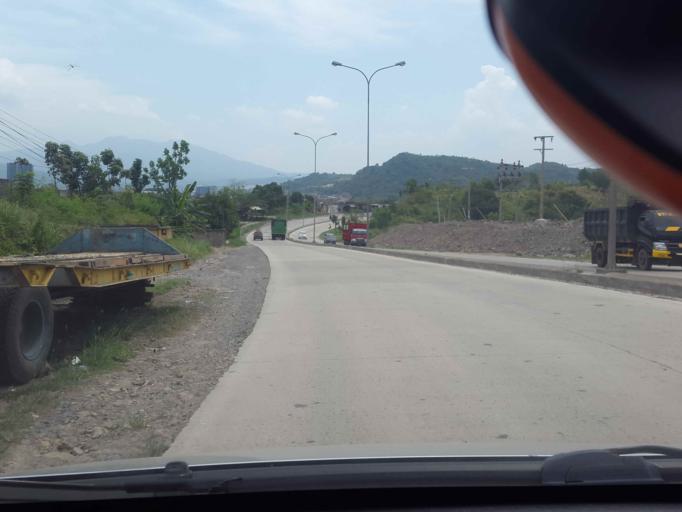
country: ID
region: Lampung
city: Panjang
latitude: -5.4385
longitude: 105.3048
